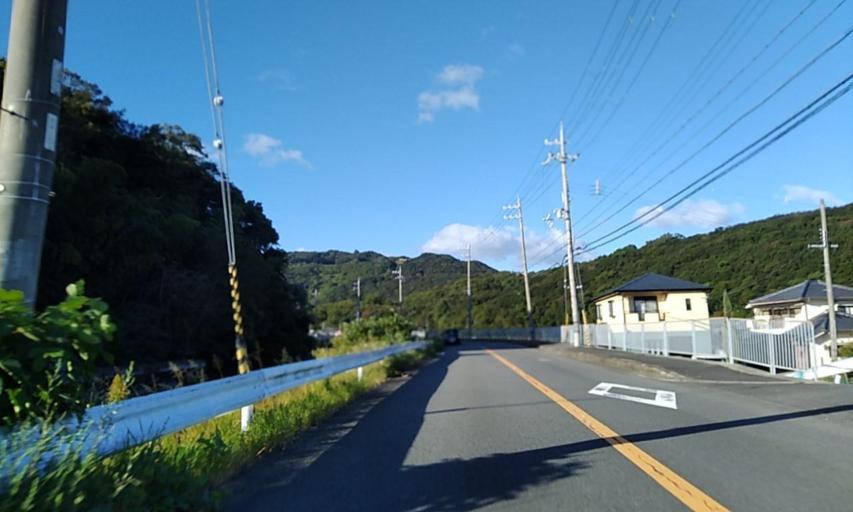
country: JP
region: Wakayama
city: Wakayama-shi
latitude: 34.3169
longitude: 135.1189
